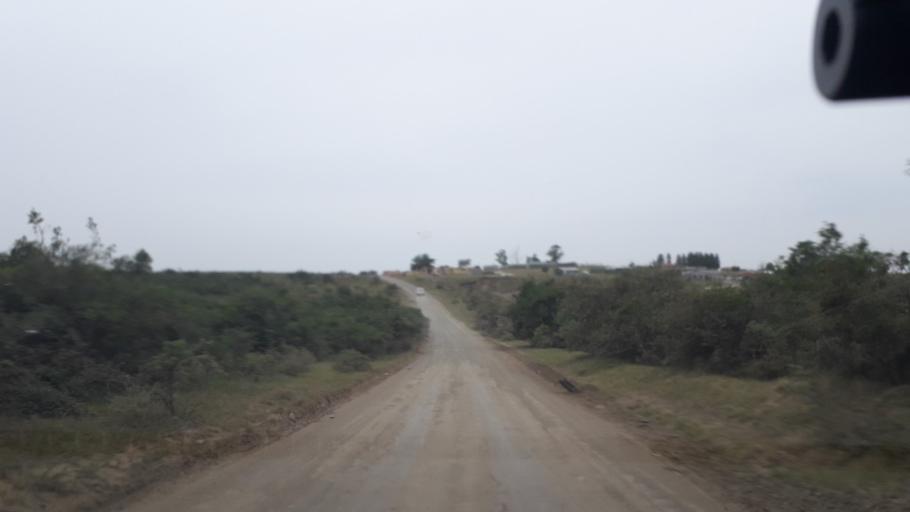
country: ZA
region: Eastern Cape
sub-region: Buffalo City Metropolitan Municipality
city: Bhisho
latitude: -32.7935
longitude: 27.3427
